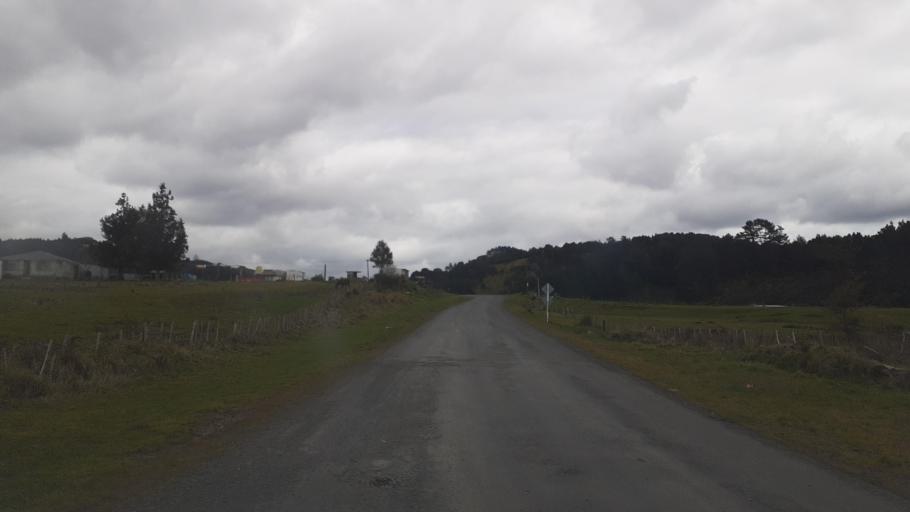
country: NZ
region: Northland
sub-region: Far North District
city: Moerewa
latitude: -35.5859
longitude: 173.9739
